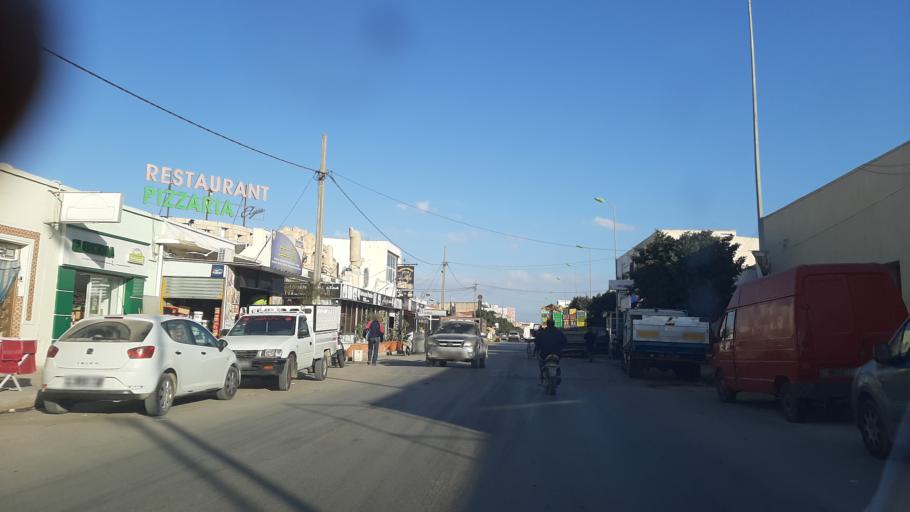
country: TN
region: Al Mahdiyah
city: El Jem
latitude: 35.2979
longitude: 10.7070
